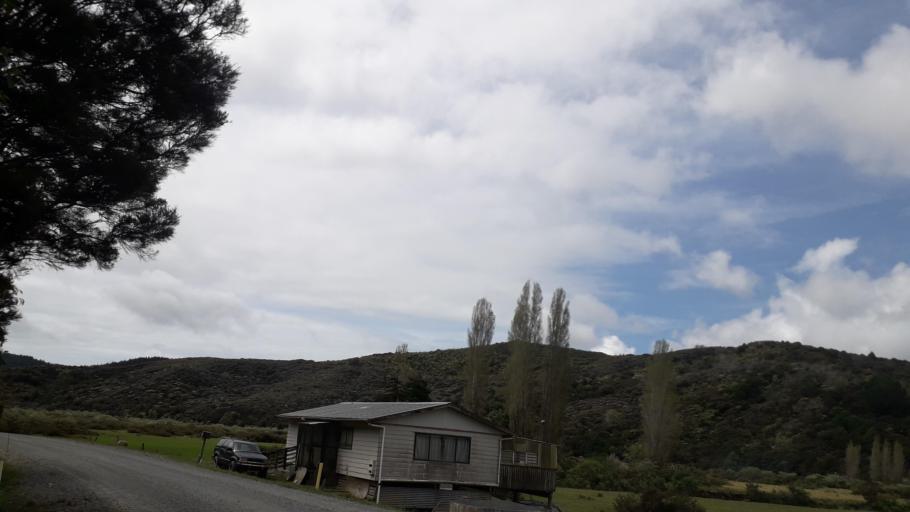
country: NZ
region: Northland
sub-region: Far North District
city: Taipa
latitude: -35.0399
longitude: 173.5650
